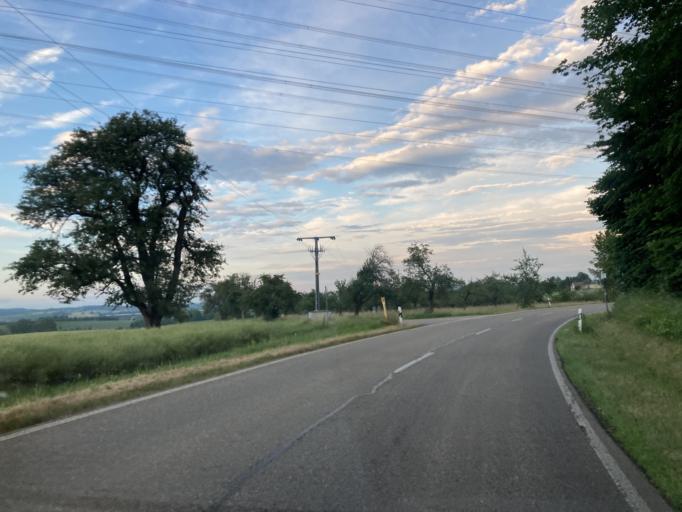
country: DE
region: Baden-Wuerttemberg
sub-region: Karlsruhe Region
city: Bretten
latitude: 49.0769
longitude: 8.7271
